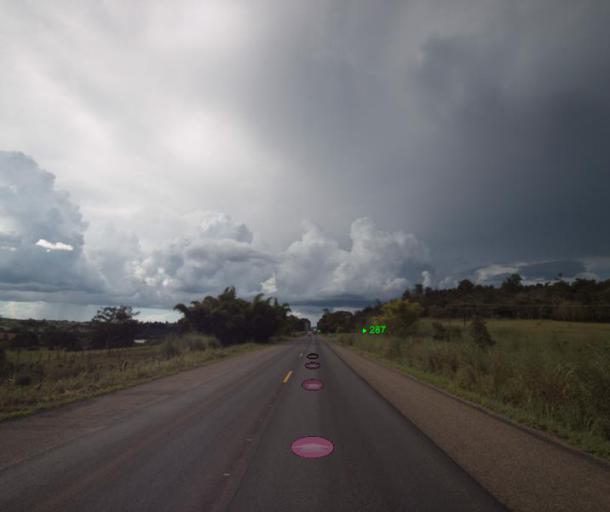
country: BR
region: Goias
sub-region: Ceres
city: Ceres
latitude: -15.1947
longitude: -49.5450
